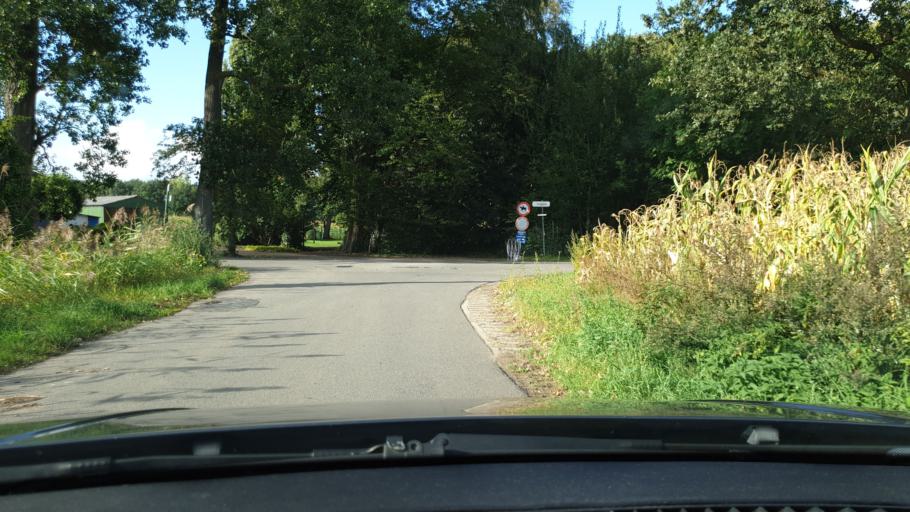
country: BE
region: Flanders
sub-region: Provincie Antwerpen
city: Geel
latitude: 51.2041
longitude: 5.0182
